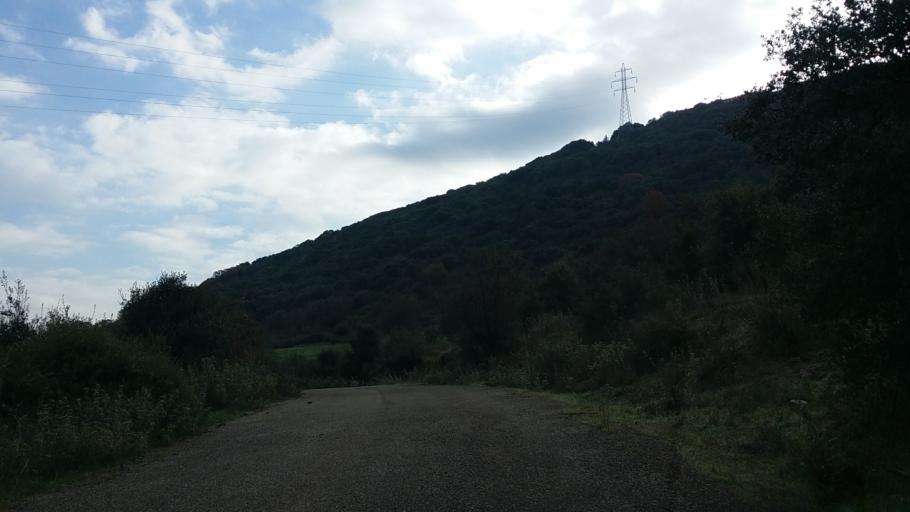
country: GR
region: West Greece
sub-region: Nomos Aitolias kai Akarnanias
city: Katouna
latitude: 38.8585
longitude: 21.0613
